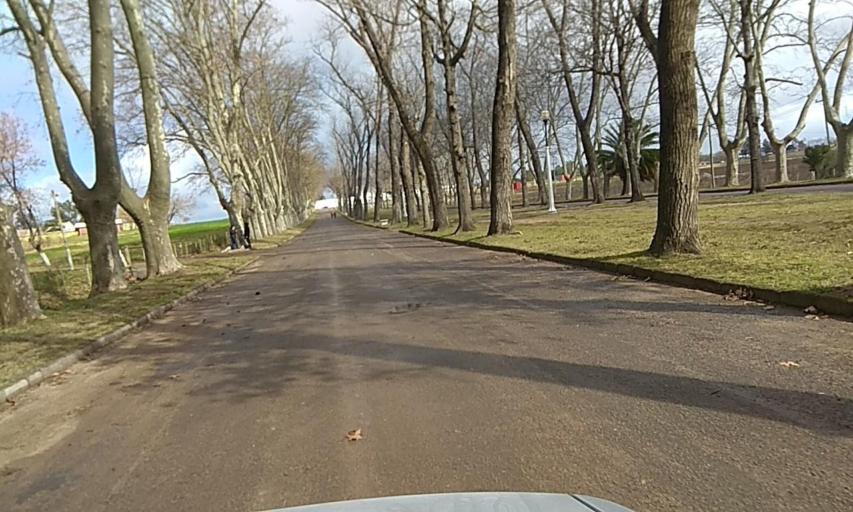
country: UY
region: Florida
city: Florida
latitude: -34.1062
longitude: -56.2256
